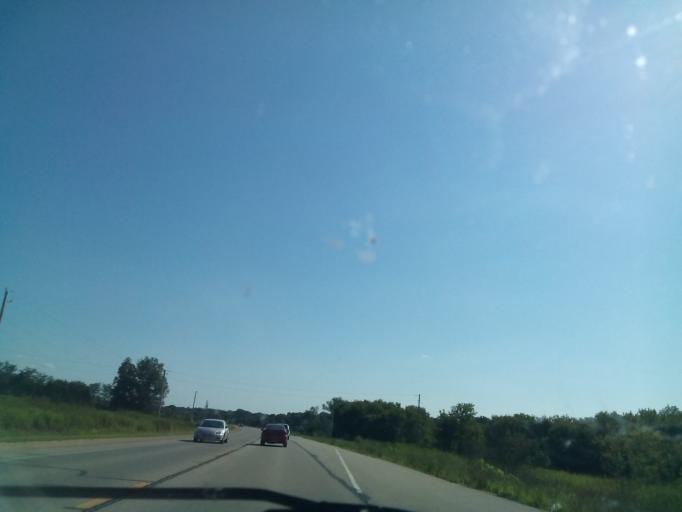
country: US
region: Wisconsin
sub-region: Green County
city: New Glarus
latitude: 42.8437
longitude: -89.6328
